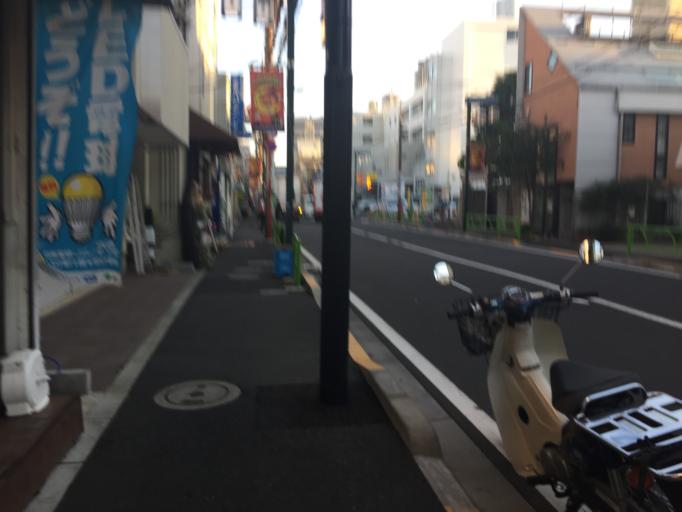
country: JP
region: Tokyo
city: Tokyo
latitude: 35.6346
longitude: 139.6603
